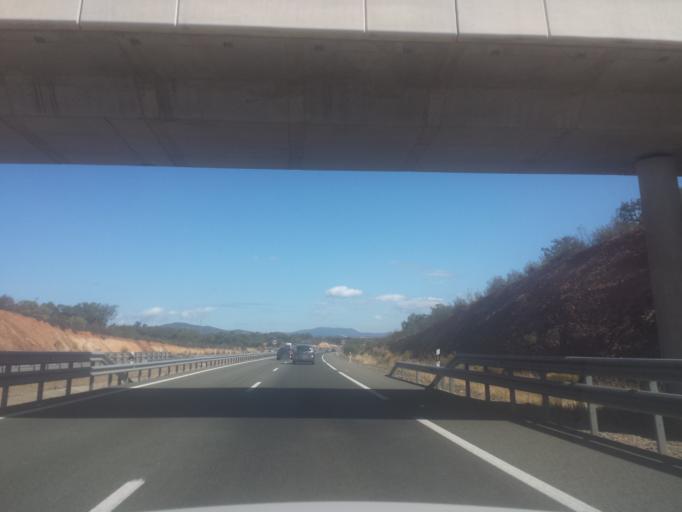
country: ES
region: Andalusia
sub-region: Provincia de Huelva
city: Santa Olalla del Cala
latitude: 37.8330
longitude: -6.2194
